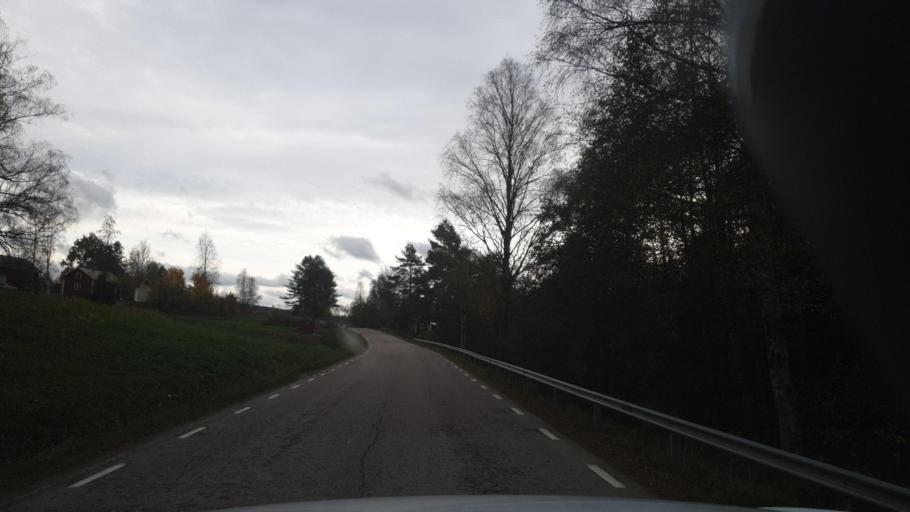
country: SE
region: Vaermland
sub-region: Arvika Kommun
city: Arvika
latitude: 59.7463
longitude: 12.8051
